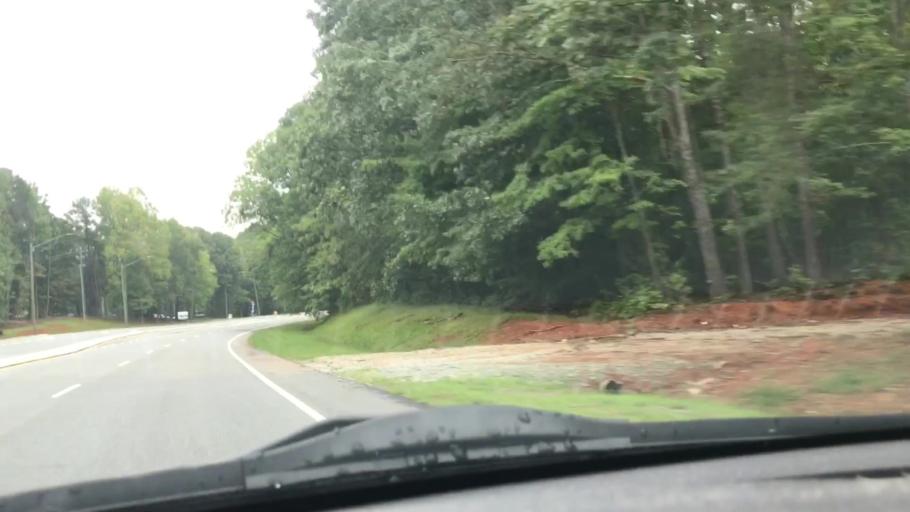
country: US
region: North Carolina
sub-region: Randolph County
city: Asheboro
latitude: 35.7342
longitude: -79.8194
